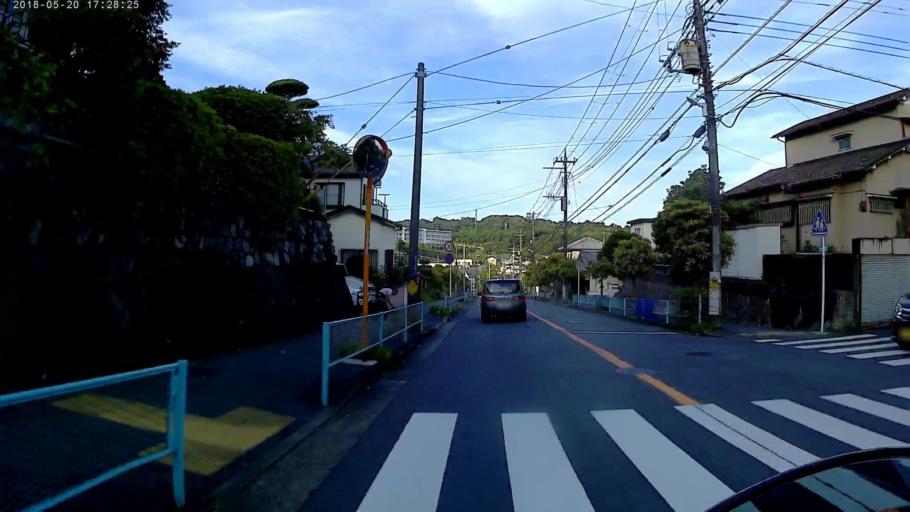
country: JP
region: Kanagawa
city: Ninomiya
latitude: 35.3121
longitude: 139.2417
